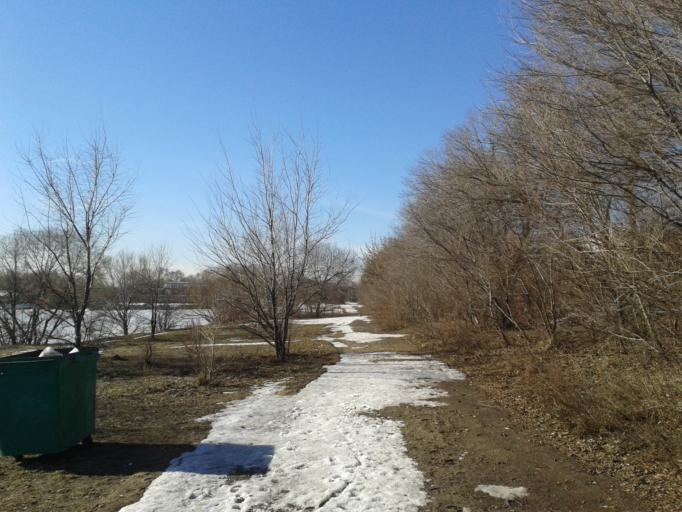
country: RU
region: Moscow
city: Strogino
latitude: 55.7999
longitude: 37.4159
